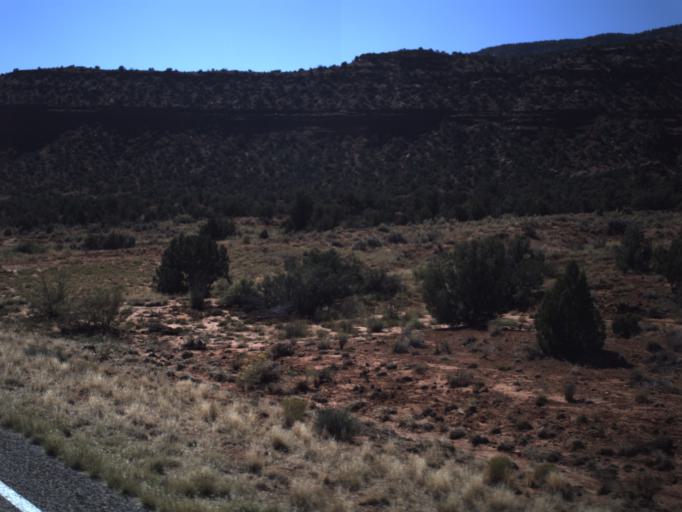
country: US
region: Utah
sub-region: San Juan County
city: Blanding
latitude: 37.6434
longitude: -110.1647
